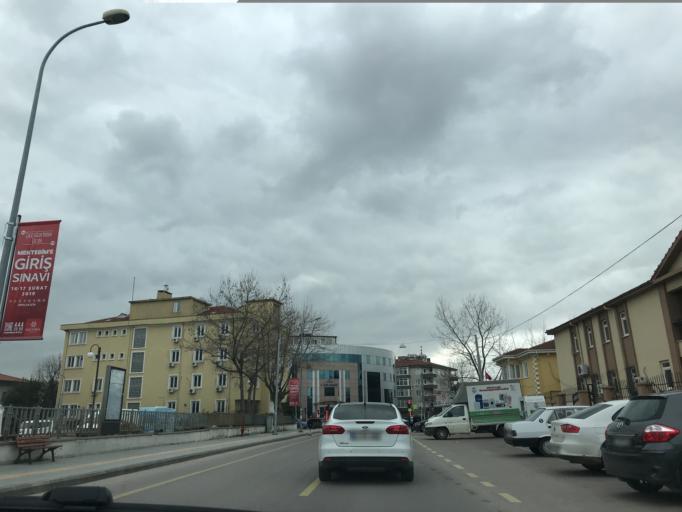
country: TR
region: Yalova
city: Yalova
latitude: 40.6531
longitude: 29.2625
